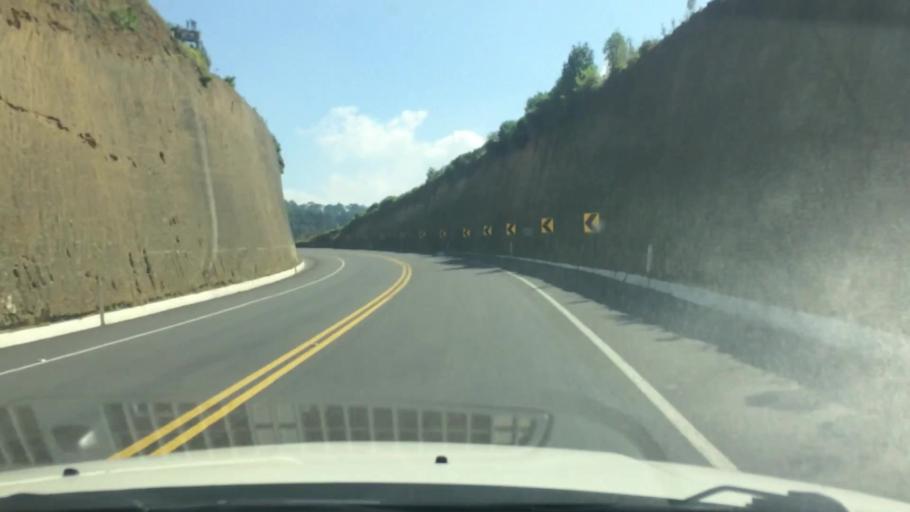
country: MX
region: Mexico
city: Amanalco de Becerra
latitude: 19.2968
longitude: -100.0143
